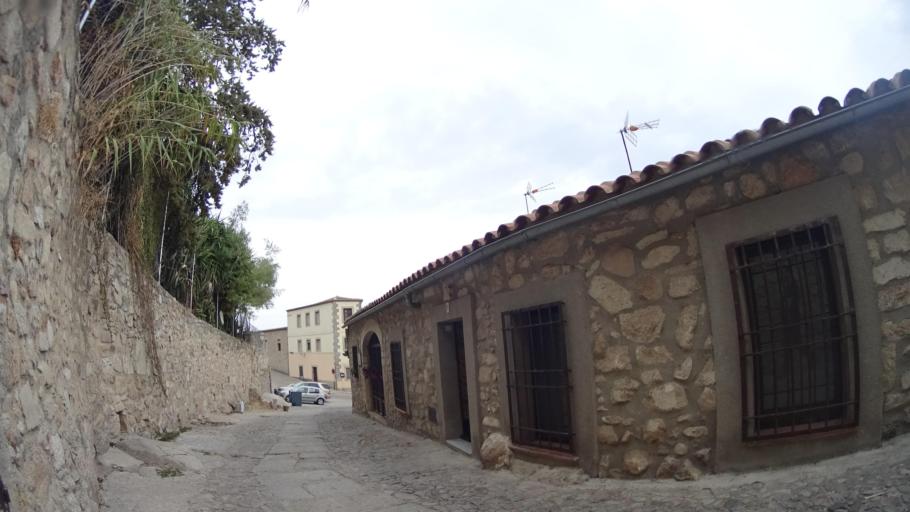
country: ES
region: Extremadura
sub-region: Provincia de Caceres
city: Trujillo
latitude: 39.4596
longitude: -5.8834
